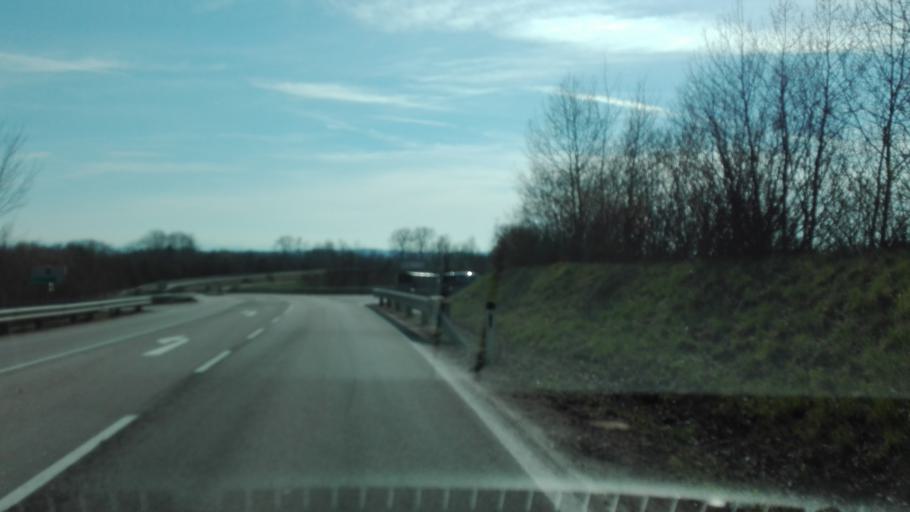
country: AT
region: Upper Austria
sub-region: Politischer Bezirk Perg
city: Perg
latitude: 48.2410
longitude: 14.6476
